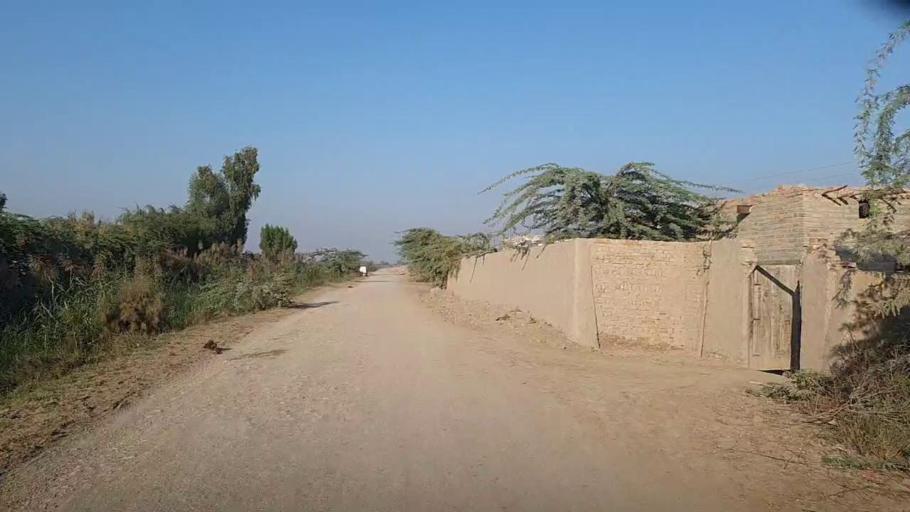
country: PK
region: Sindh
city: Ranipur
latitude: 27.2524
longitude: 68.5079
